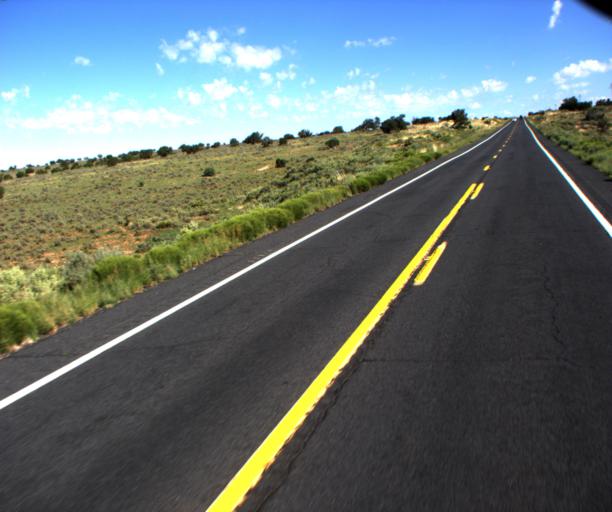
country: US
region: Arizona
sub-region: Coconino County
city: Grand Canyon Village
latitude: 35.7334
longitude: -112.1311
